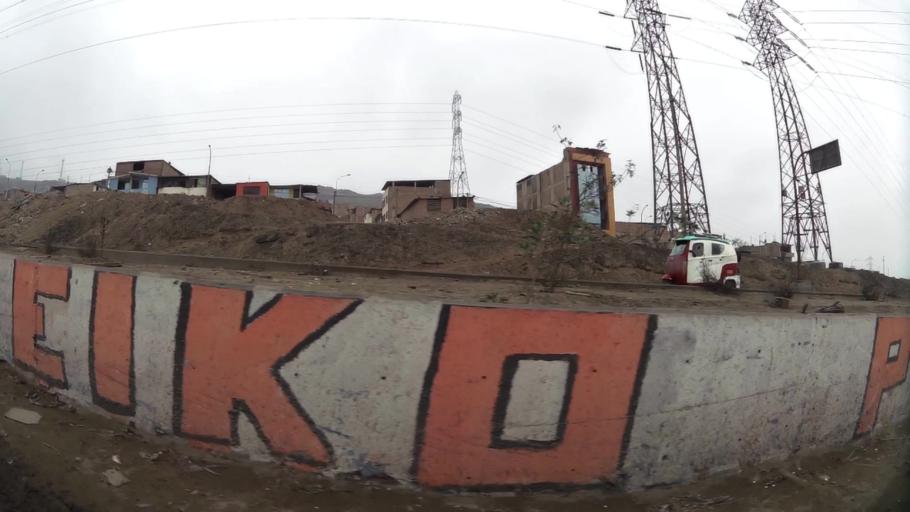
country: PE
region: Lima
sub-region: Lima
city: Surco
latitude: -12.2153
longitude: -76.9221
